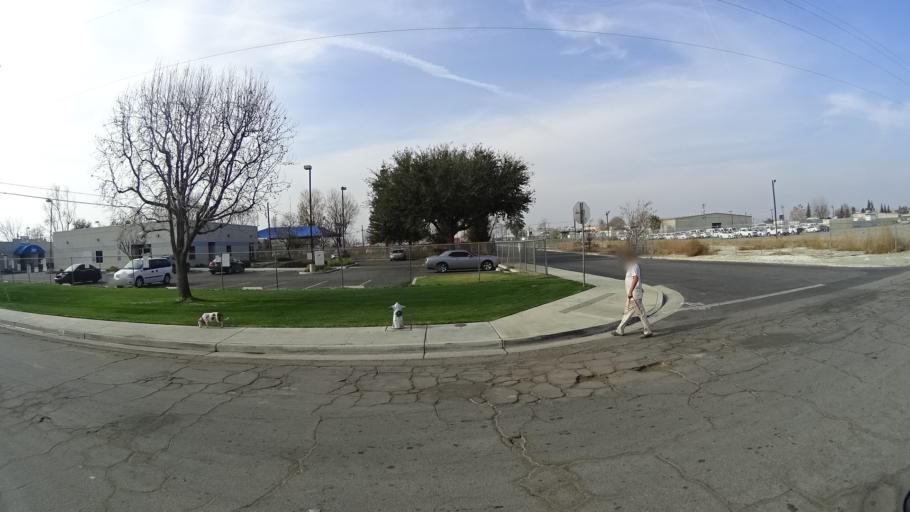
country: US
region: California
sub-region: Kern County
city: Bakersfield
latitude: 35.3700
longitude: -118.9987
